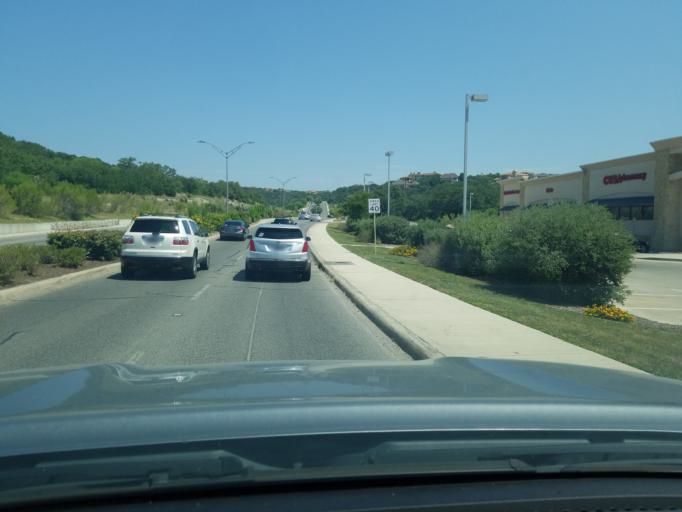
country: US
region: Texas
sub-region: Bexar County
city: Hollywood Park
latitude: 29.6434
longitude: -98.4810
